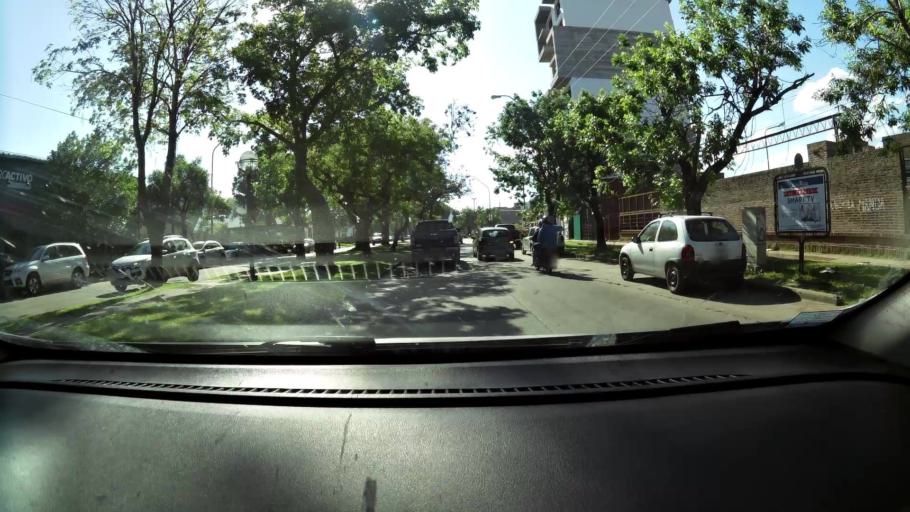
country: AR
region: Santa Fe
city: Santa Fe de la Vera Cruz
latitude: -31.6063
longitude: -60.6888
